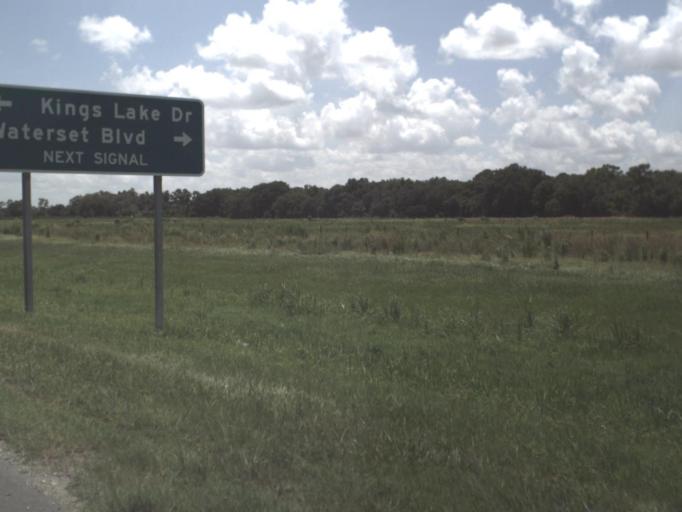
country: US
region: Florida
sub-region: Hillsborough County
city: Apollo Beach
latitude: 27.7923
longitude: -82.3767
